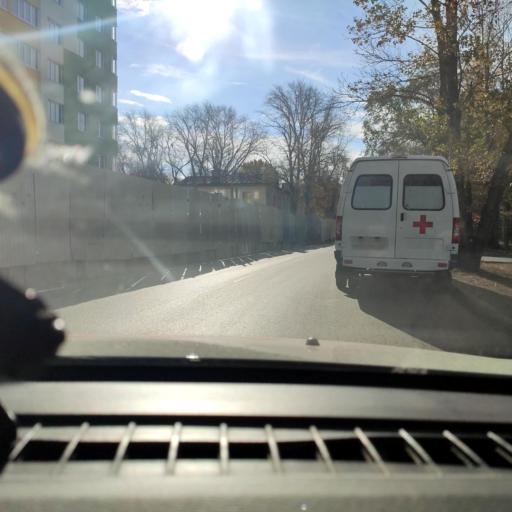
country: RU
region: Samara
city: Samara
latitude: 53.2051
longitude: 50.1739
